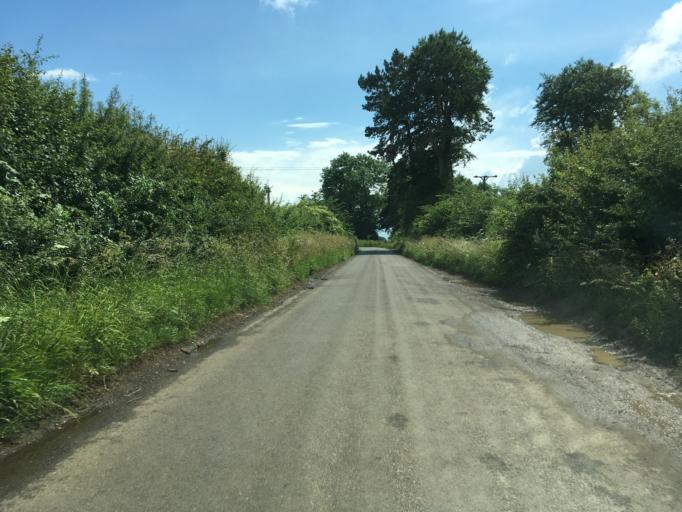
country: GB
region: England
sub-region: Gloucestershire
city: Tetbury
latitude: 51.6755
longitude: -2.1461
